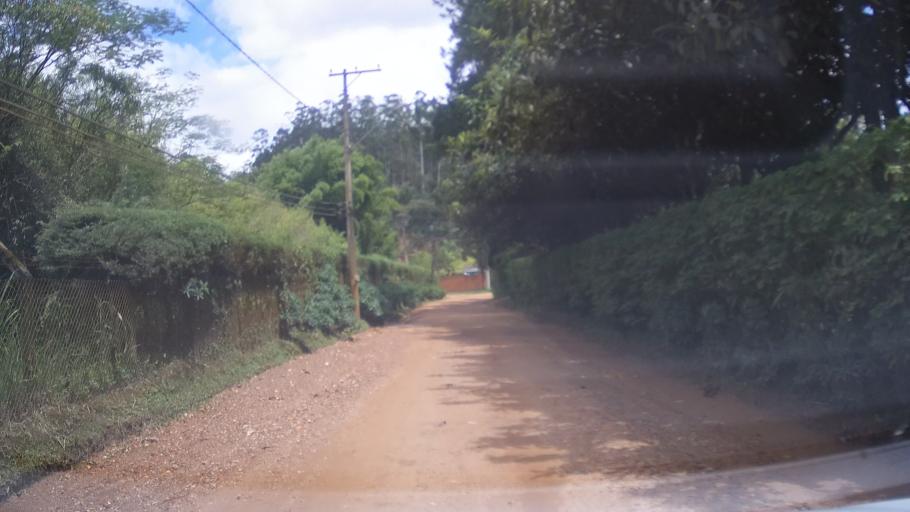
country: BR
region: Sao Paulo
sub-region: Campo Limpo Paulista
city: Campo Limpo Paulista
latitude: -23.2011
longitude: -46.7215
